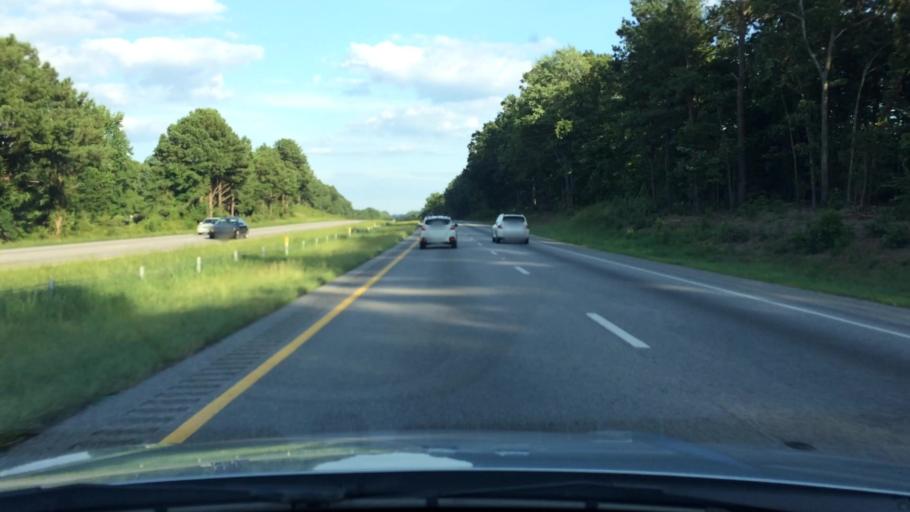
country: US
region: South Carolina
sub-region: Laurens County
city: Joanna
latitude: 34.4637
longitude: -81.7997
